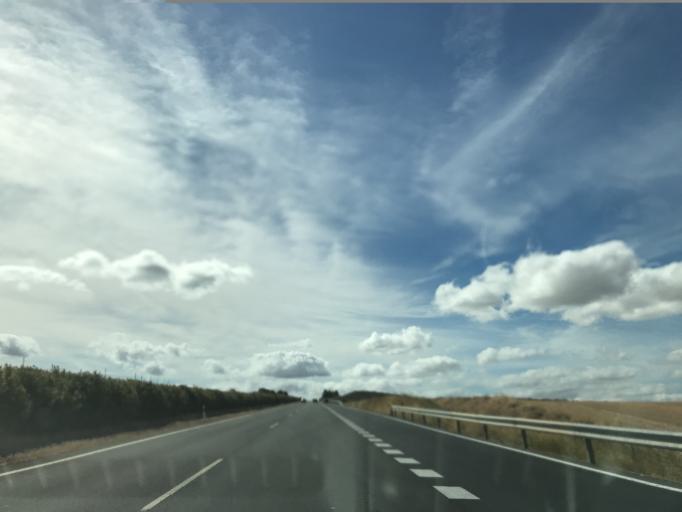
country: ES
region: Andalusia
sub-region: Province of Cordoba
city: La Victoria
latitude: 37.7293
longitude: -4.8554
